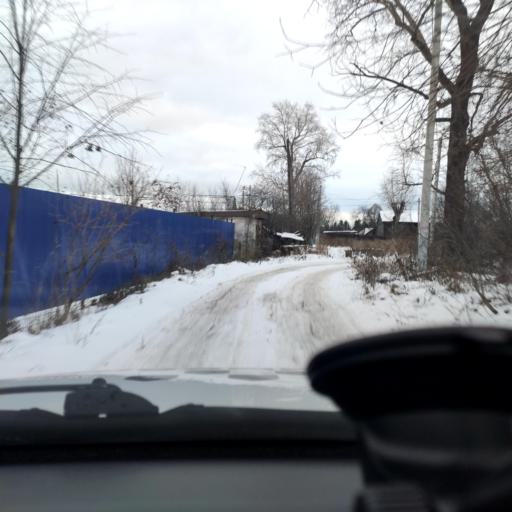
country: RU
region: Perm
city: Froly
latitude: 57.9541
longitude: 56.2873
